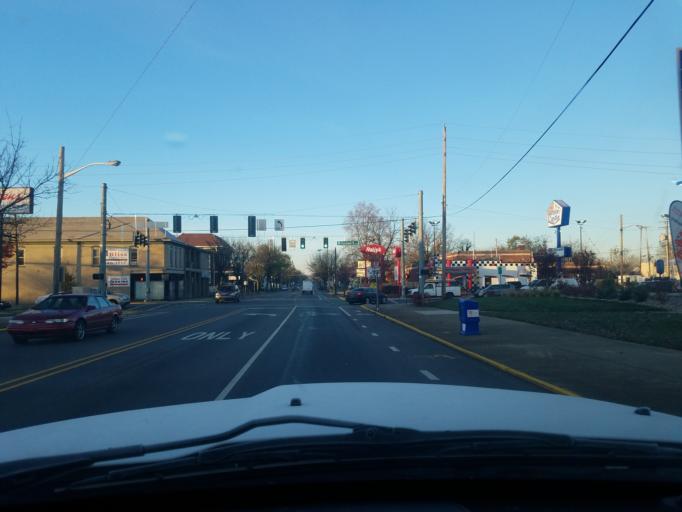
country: US
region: Indiana
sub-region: Floyd County
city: New Albany
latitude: 38.2929
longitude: -85.8067
